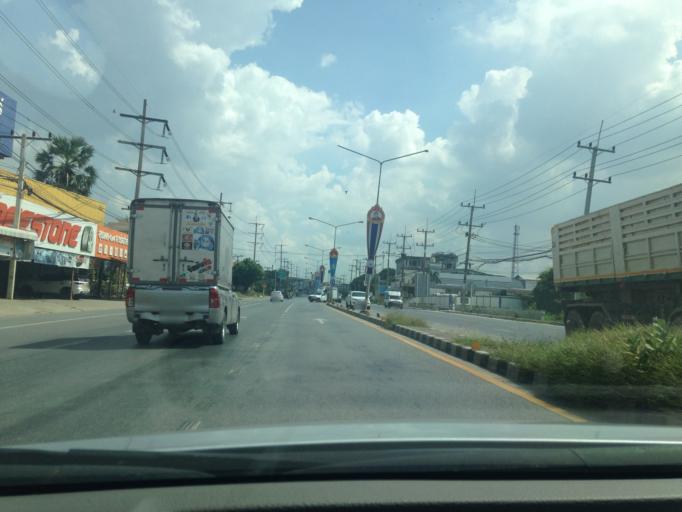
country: TH
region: Pathum Thani
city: Sam Khok
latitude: 14.0743
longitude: 100.5210
